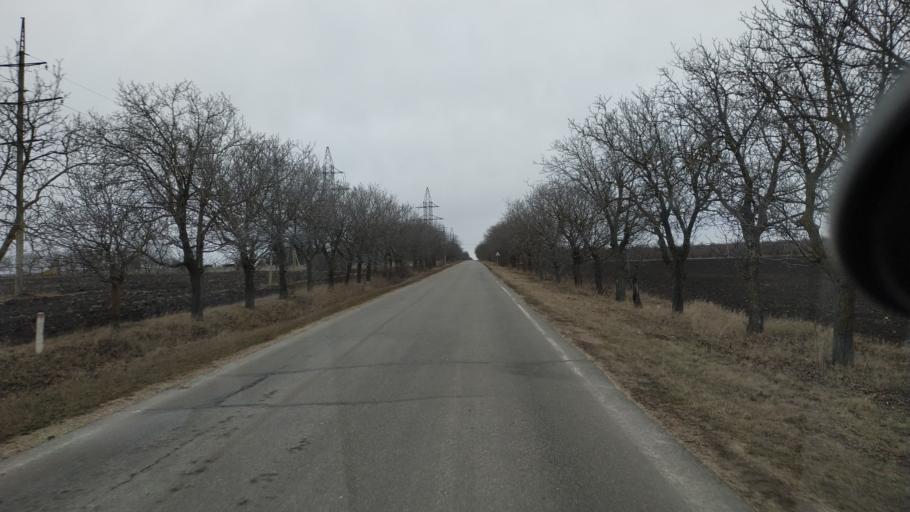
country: MD
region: Telenesti
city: Cocieri
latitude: 47.3318
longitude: 29.0512
